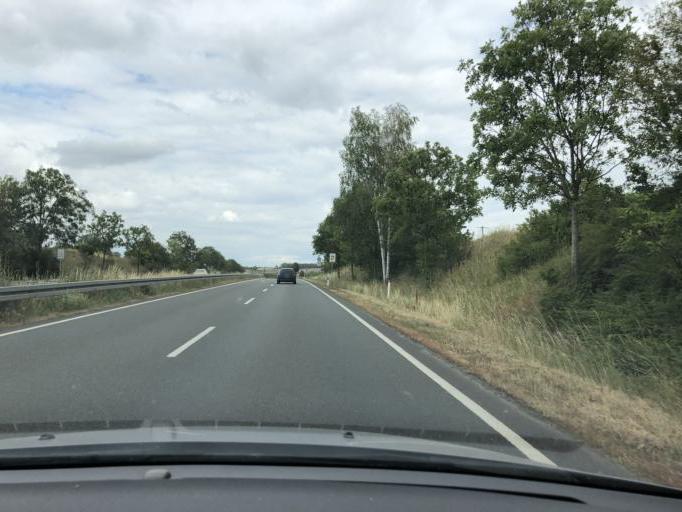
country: DE
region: Saxony-Anhalt
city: Wansleben
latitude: 51.4727
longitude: 11.7565
